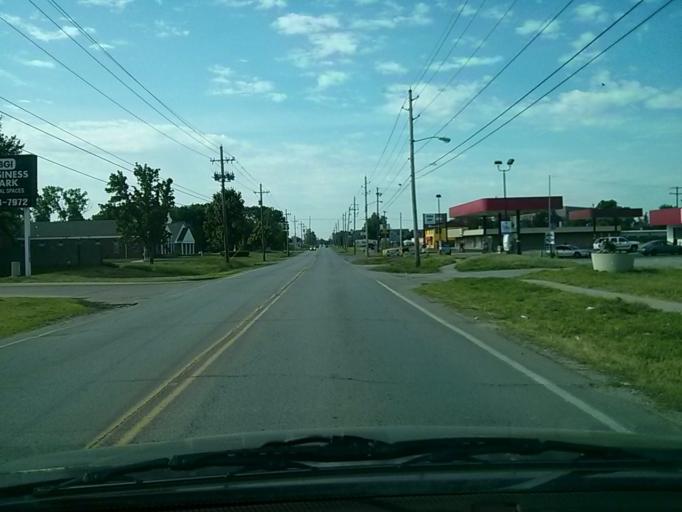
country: US
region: Oklahoma
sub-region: Tulsa County
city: Jenks
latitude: 36.0716
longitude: -95.9758
